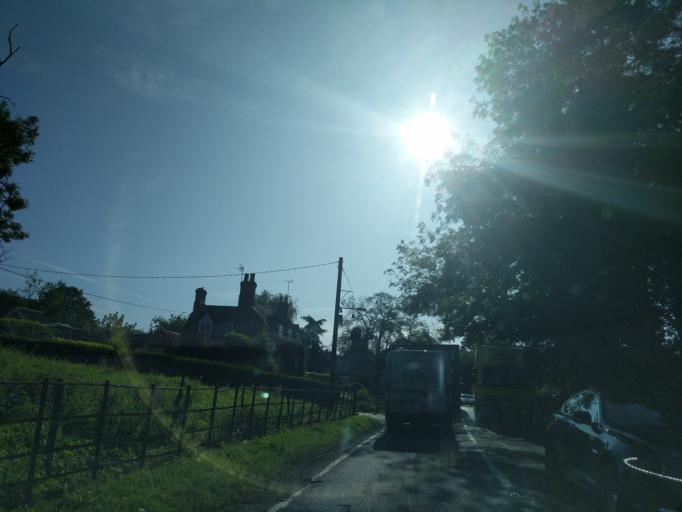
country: GB
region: England
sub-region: Lincolnshire
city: Bourne
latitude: 52.7945
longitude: -0.4483
